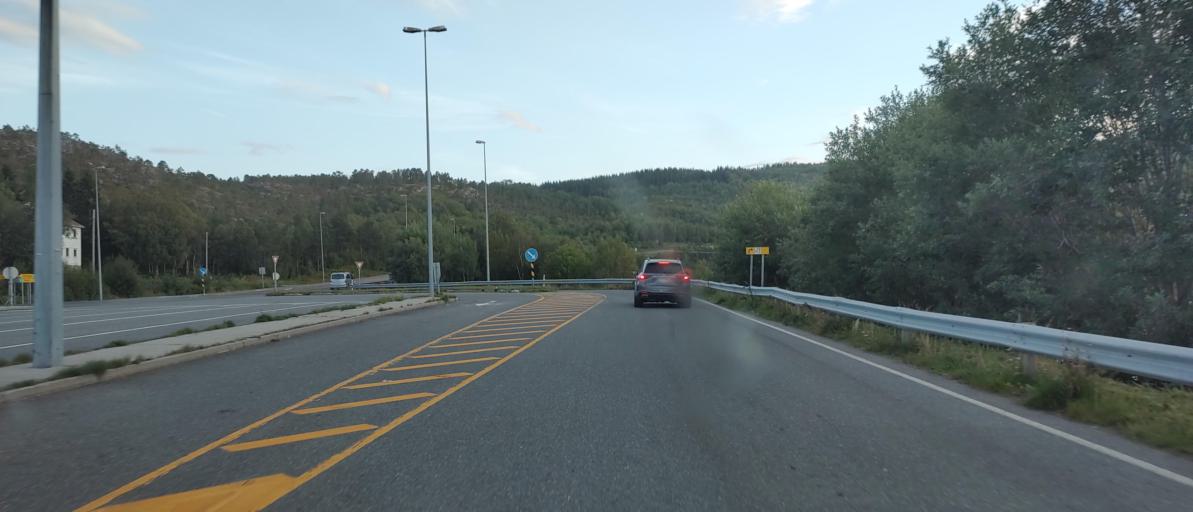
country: NO
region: Nordland
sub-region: Lodingen
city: Lodingen
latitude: 68.2223
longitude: 16.0713
